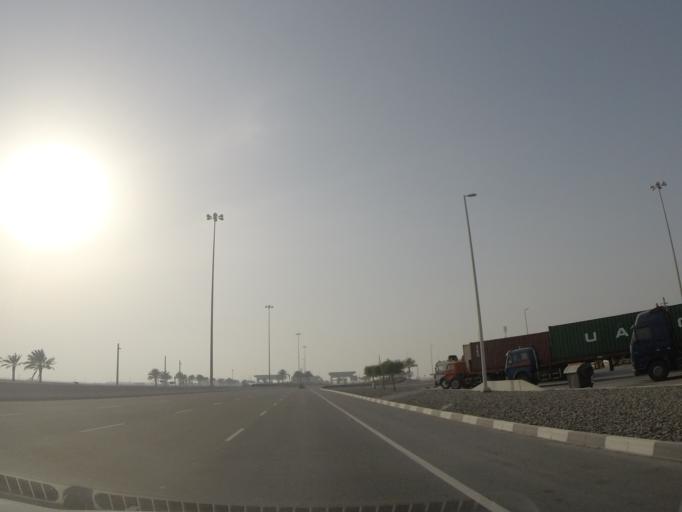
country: AE
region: Abu Dhabi
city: Abu Dhabi
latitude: 24.7793
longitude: 54.7073
